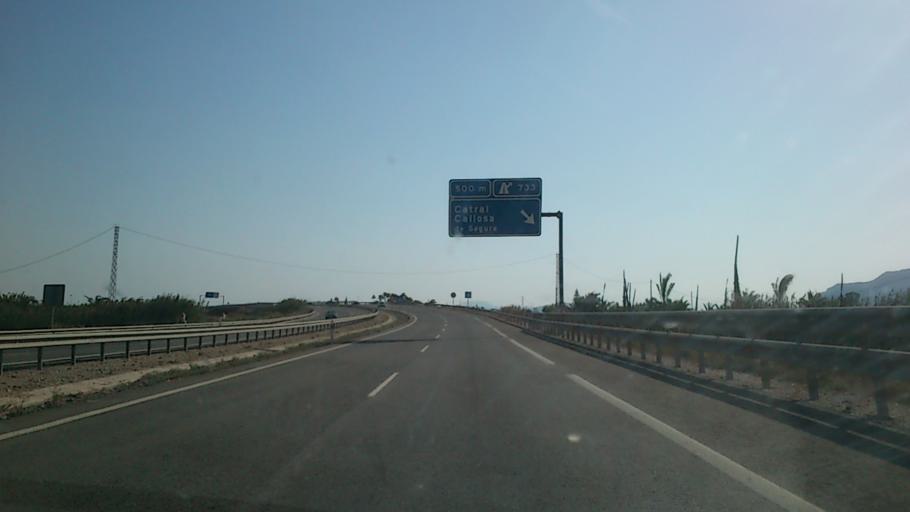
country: ES
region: Valencia
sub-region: Provincia de Alicante
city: Catral
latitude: 38.1553
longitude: -0.8180
